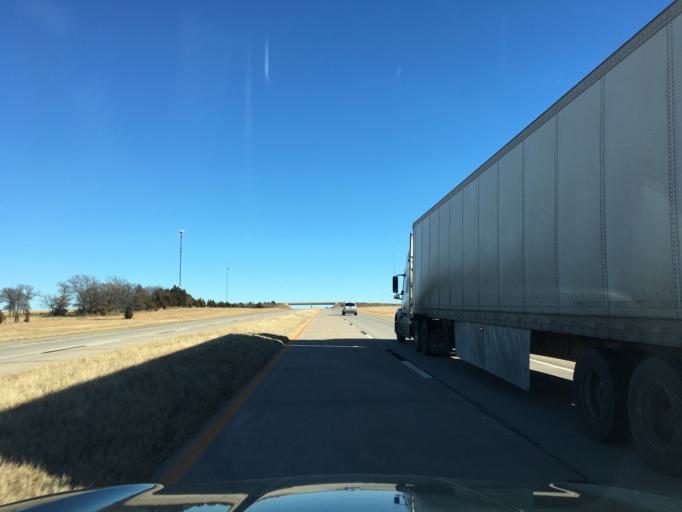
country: US
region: Oklahoma
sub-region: Payne County
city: Yale
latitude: 36.2243
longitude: -96.7549
